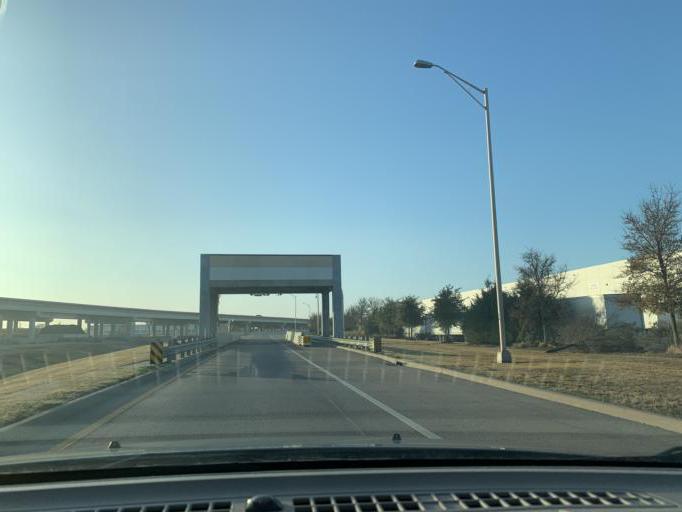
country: US
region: Texas
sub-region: Dallas County
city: Carrollton
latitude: 32.9504
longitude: -96.9269
